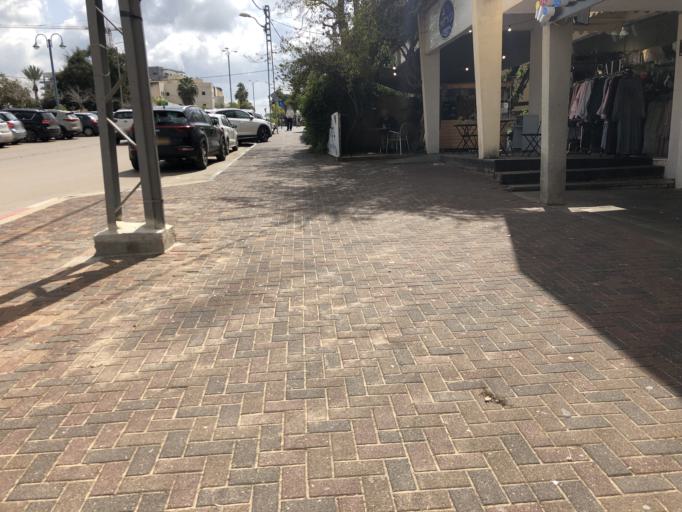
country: IL
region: Haifa
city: Hadera
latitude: 32.4756
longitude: 34.9723
